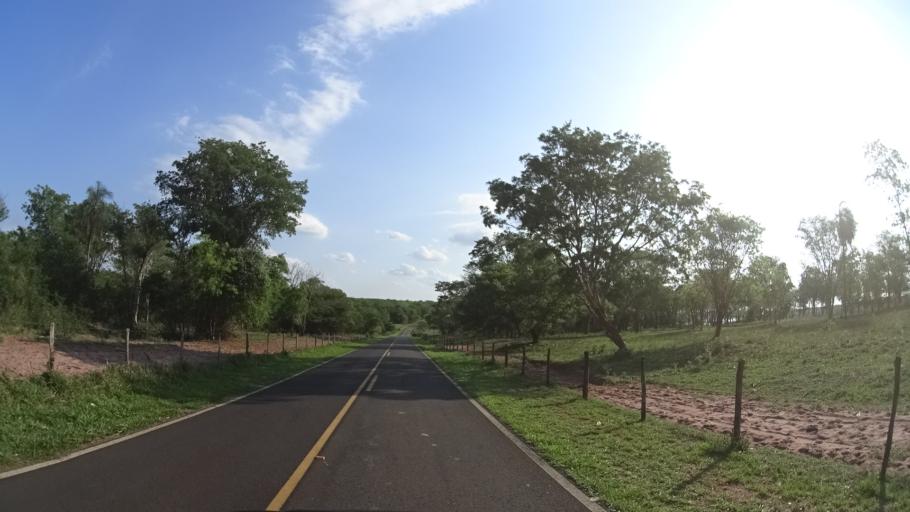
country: BR
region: Sao Paulo
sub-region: Urupes
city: Urupes
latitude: -21.3997
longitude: -49.5154
